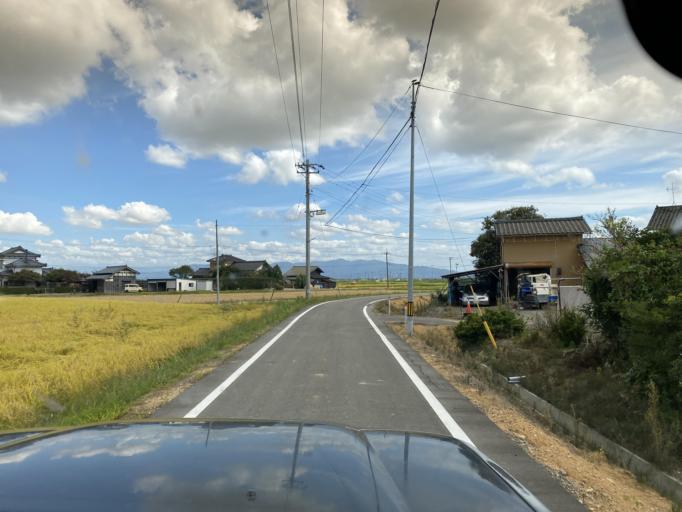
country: JP
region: Niigata
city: Niitsu-honcho
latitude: 37.8174
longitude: 139.0791
